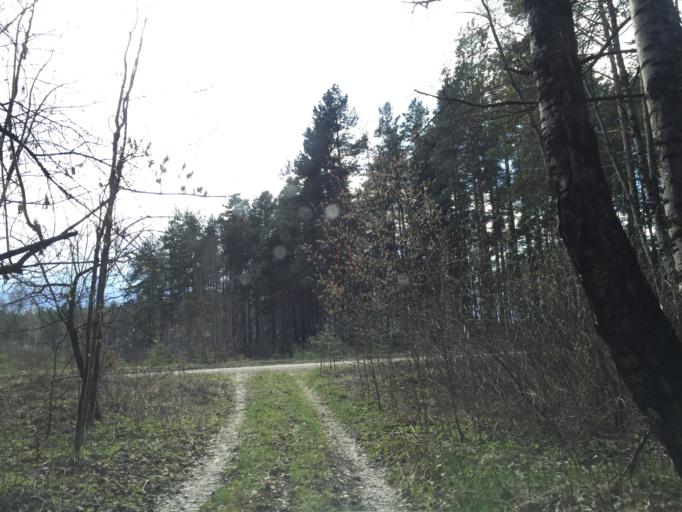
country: LV
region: Riga
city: Bergi
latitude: 56.9997
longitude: 24.2963
